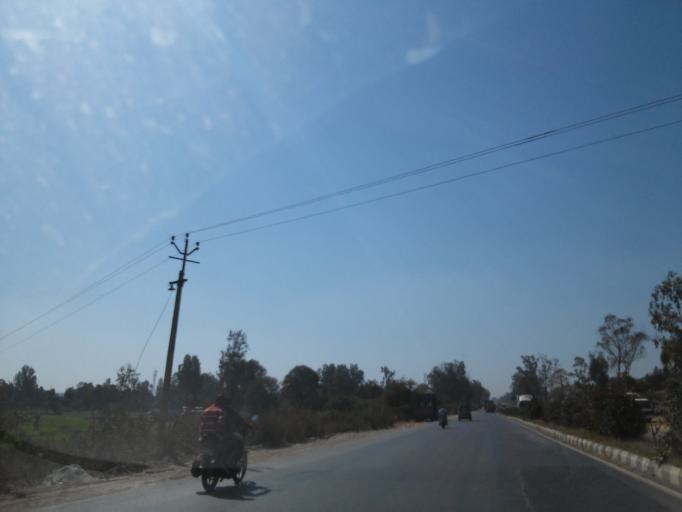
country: IN
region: Rajasthan
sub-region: Dungarpur
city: Dungarpur
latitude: 23.7941
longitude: 73.5234
